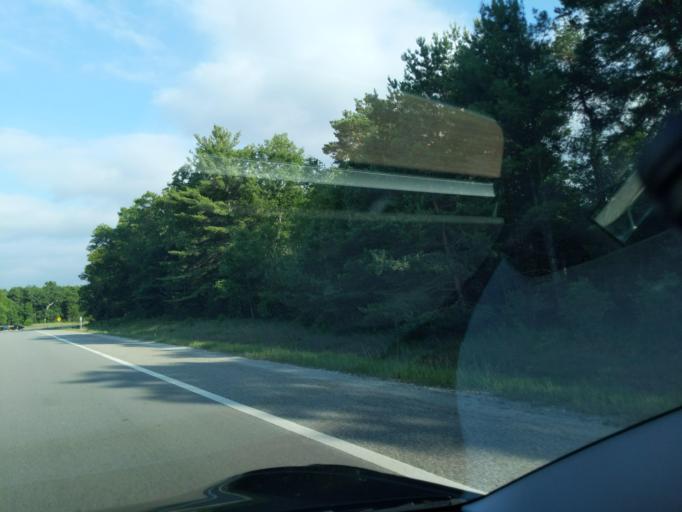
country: US
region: Michigan
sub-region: Muskegon County
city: Lakewood Club
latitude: 43.3826
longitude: -86.2821
